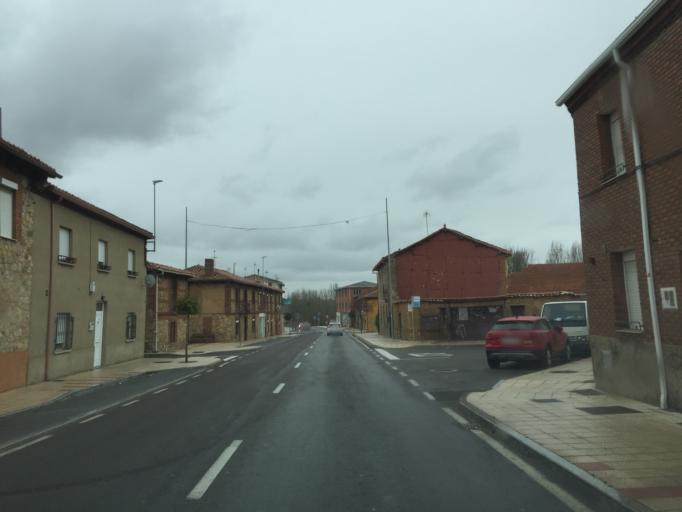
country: ES
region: Castille and Leon
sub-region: Provincia de Leon
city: Sariegos
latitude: 42.6676
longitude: -5.6299
